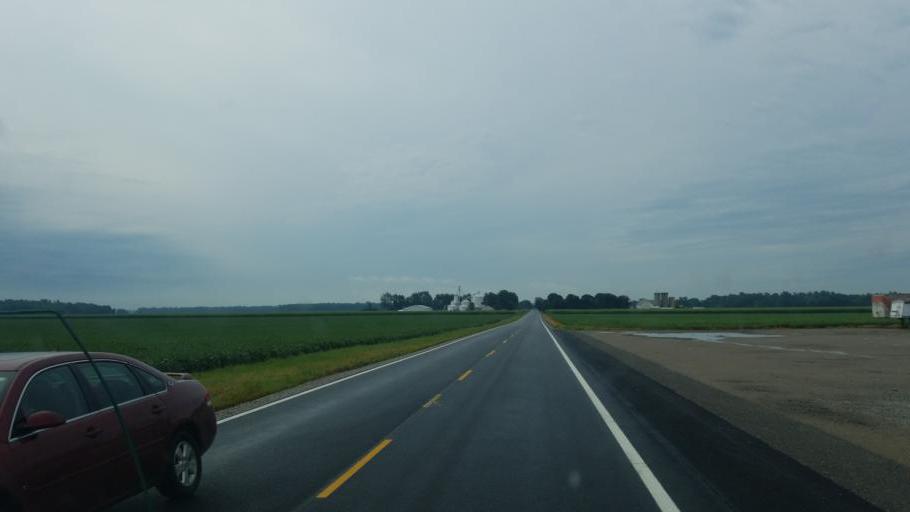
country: US
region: Ohio
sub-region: Williams County
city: Edgerton
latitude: 41.3724
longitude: -84.6696
